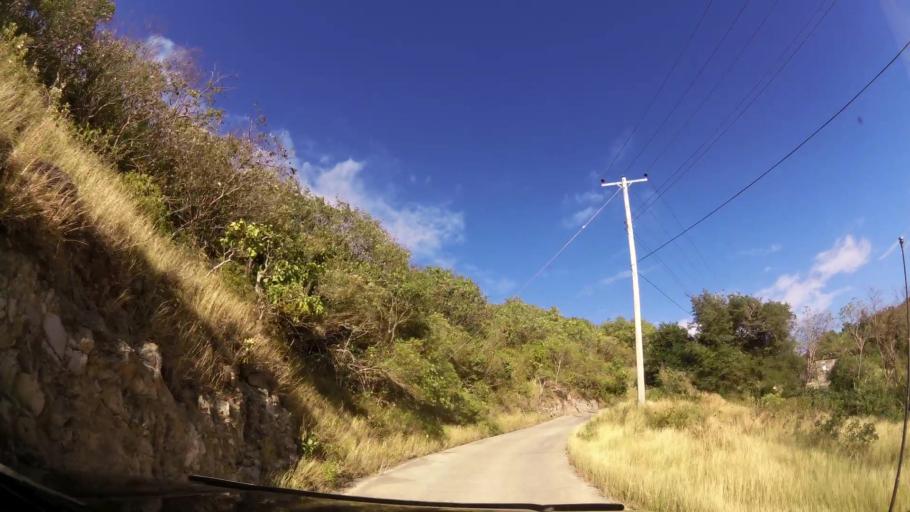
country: MS
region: Saint Peter
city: Brades
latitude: 16.8035
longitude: -62.1944
